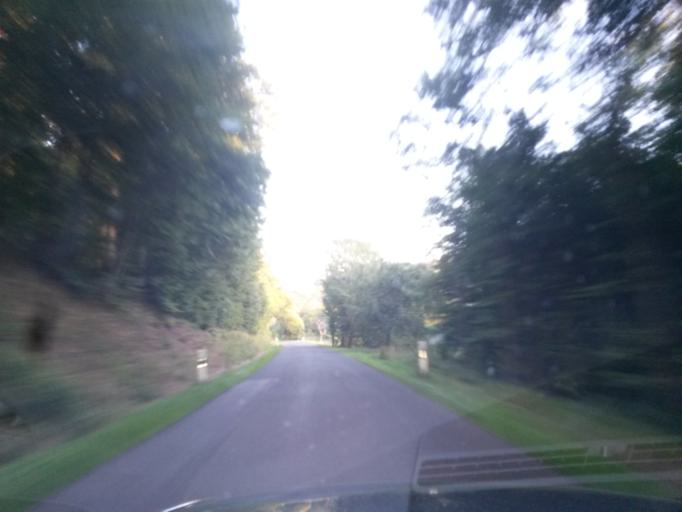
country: DE
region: Bavaria
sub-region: Regierungsbezirk Unterfranken
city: Rechtenbach
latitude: 49.9481
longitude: 9.4725
